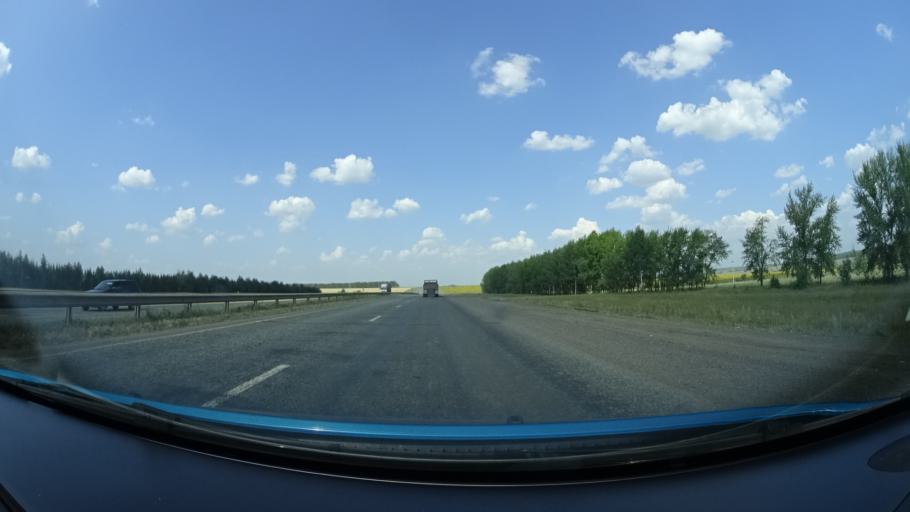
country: RU
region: Bashkortostan
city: Dmitriyevka
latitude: 54.6801
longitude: 55.3373
